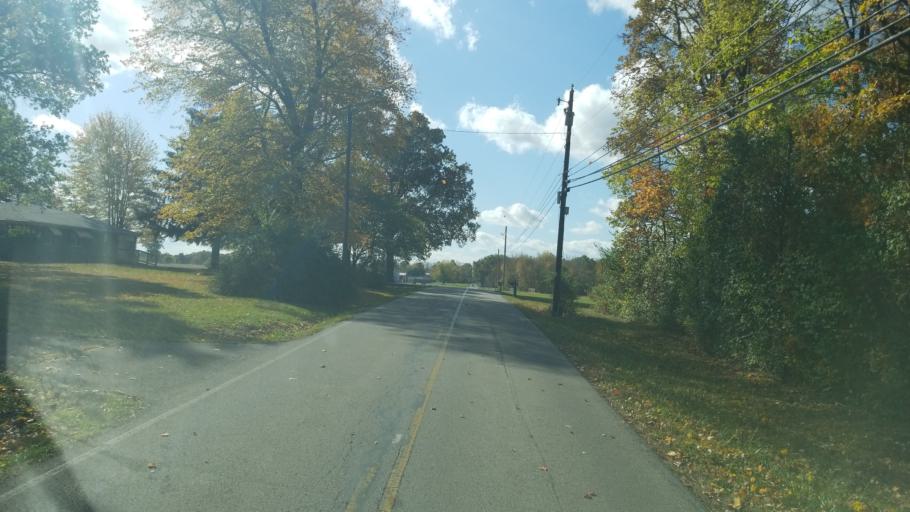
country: US
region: Ohio
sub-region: Warren County
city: Morrow
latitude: 39.4053
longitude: -84.1524
